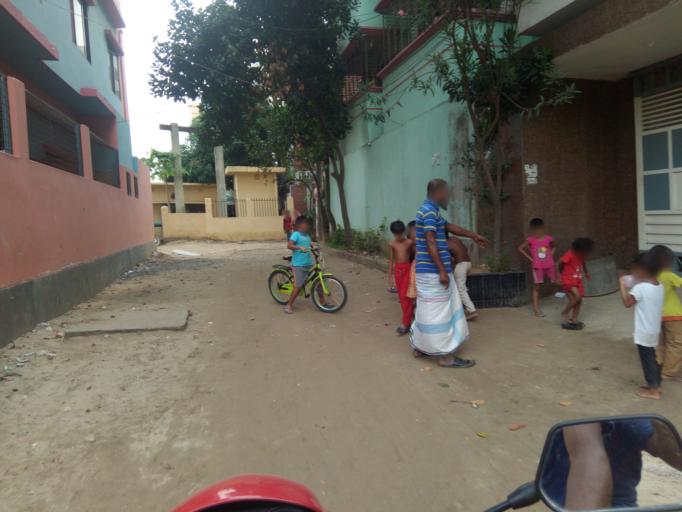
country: BD
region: Dhaka
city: Paltan
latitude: 23.7593
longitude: 90.4303
